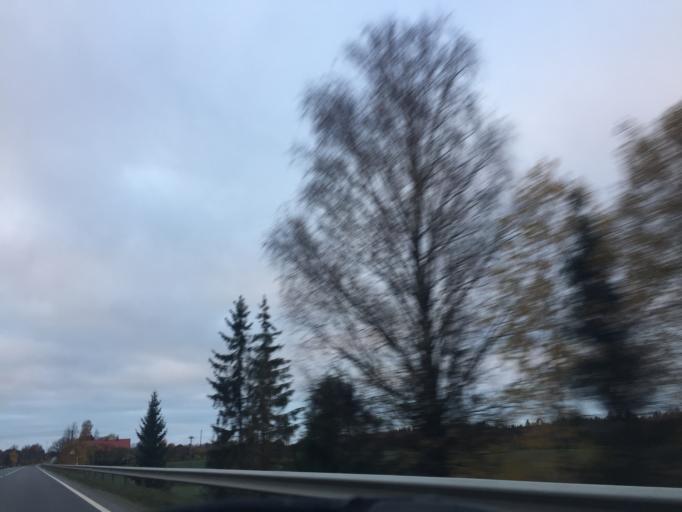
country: LV
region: Aizpute
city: Aizpute
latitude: 56.5884
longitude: 21.6680
